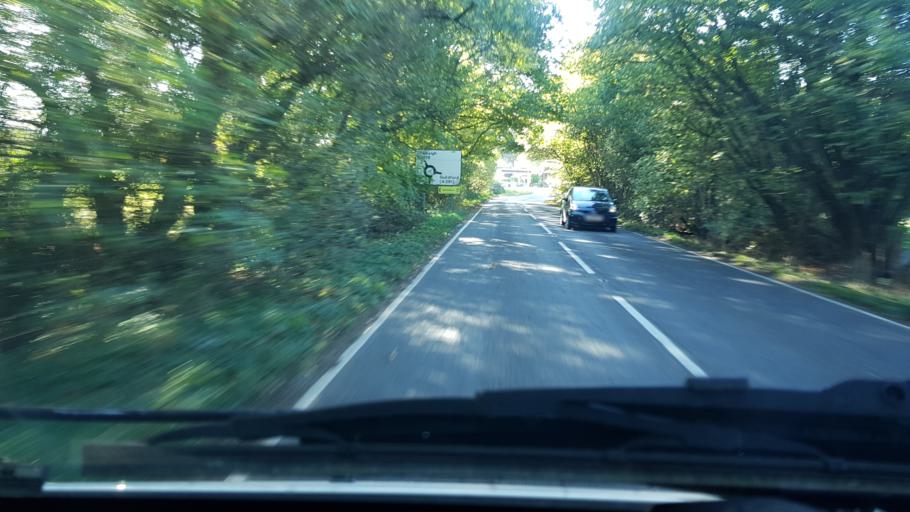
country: GB
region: England
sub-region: Surrey
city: Cranleigh
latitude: 51.1667
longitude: -0.5112
